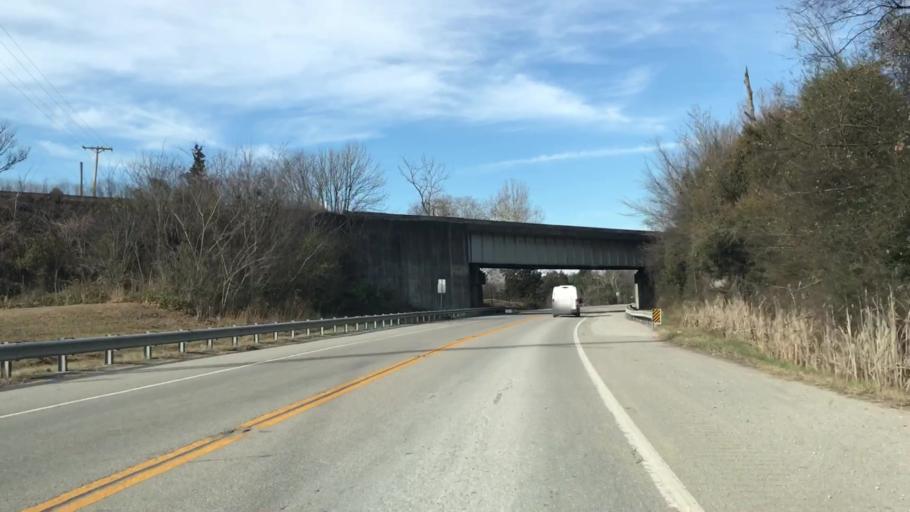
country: US
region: Kentucky
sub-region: Pulaski County
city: Somerset
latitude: 36.9540
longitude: -84.5801
